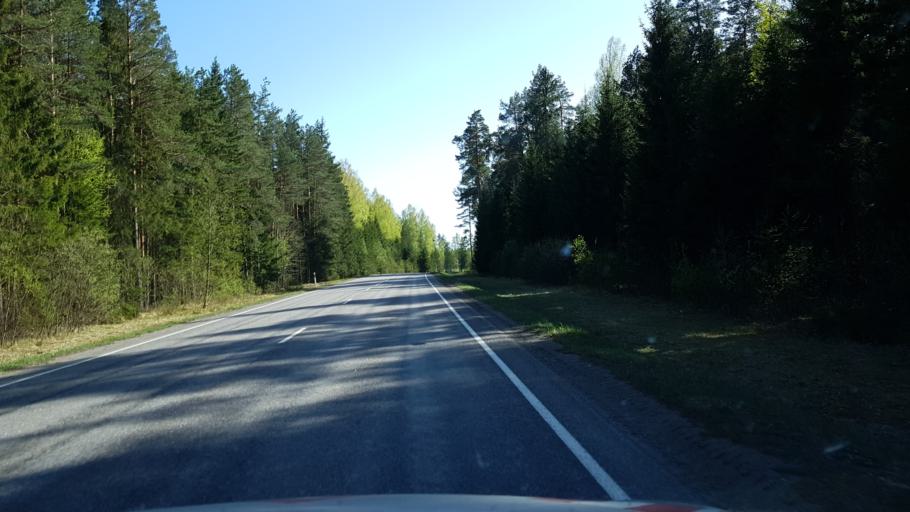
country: EE
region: Paernumaa
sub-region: Saarde vald
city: Kilingi-Nomme
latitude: 58.1861
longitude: 25.0541
